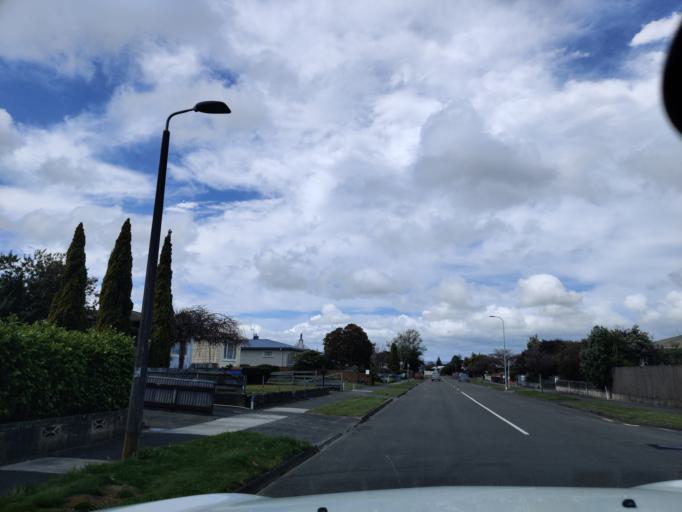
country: NZ
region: Manawatu-Wanganui
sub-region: Palmerston North City
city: Palmerston North
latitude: -40.3606
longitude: 175.5819
